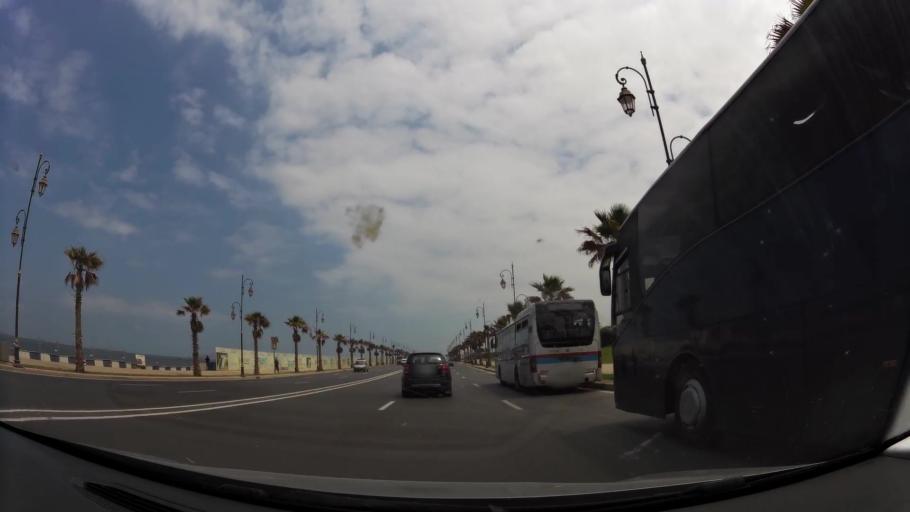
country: MA
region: Rabat-Sale-Zemmour-Zaer
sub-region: Rabat
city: Rabat
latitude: 33.9884
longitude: -6.8874
